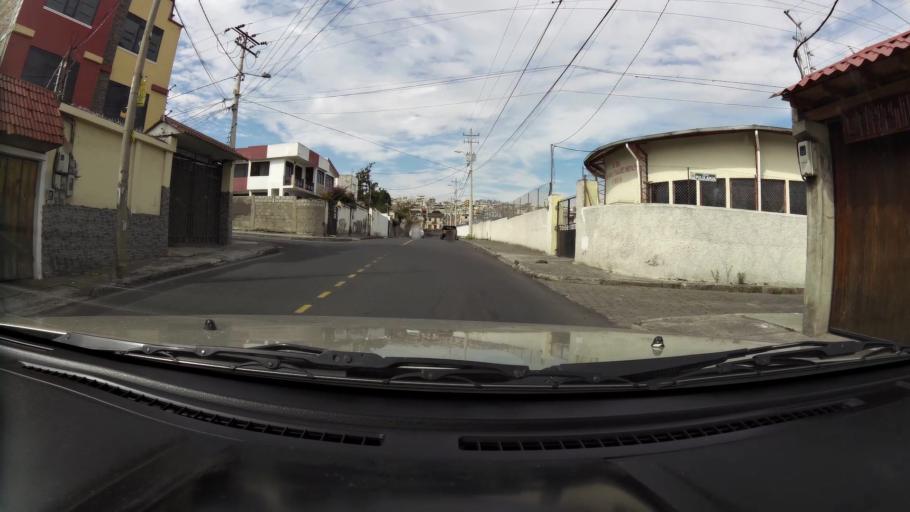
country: EC
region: Tungurahua
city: Ambato
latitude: -1.2451
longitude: -78.6203
